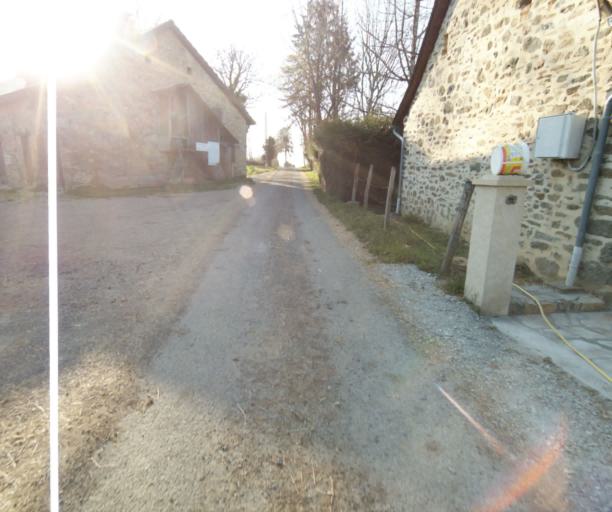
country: FR
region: Limousin
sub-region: Departement de la Correze
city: Saint-Clement
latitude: 45.3361
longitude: 1.6556
